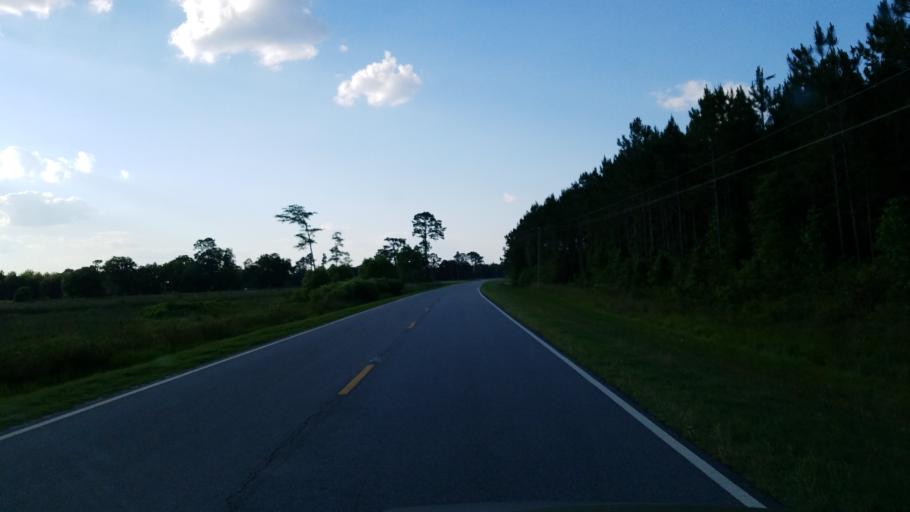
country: US
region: Georgia
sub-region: Lanier County
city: Lakeland
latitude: 31.1290
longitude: -83.0854
